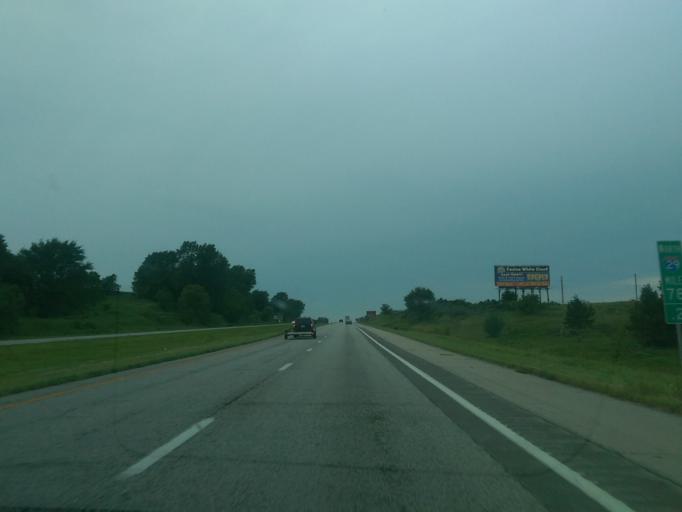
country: US
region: Missouri
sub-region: Holt County
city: Mound City
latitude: 40.0661
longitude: -95.1767
